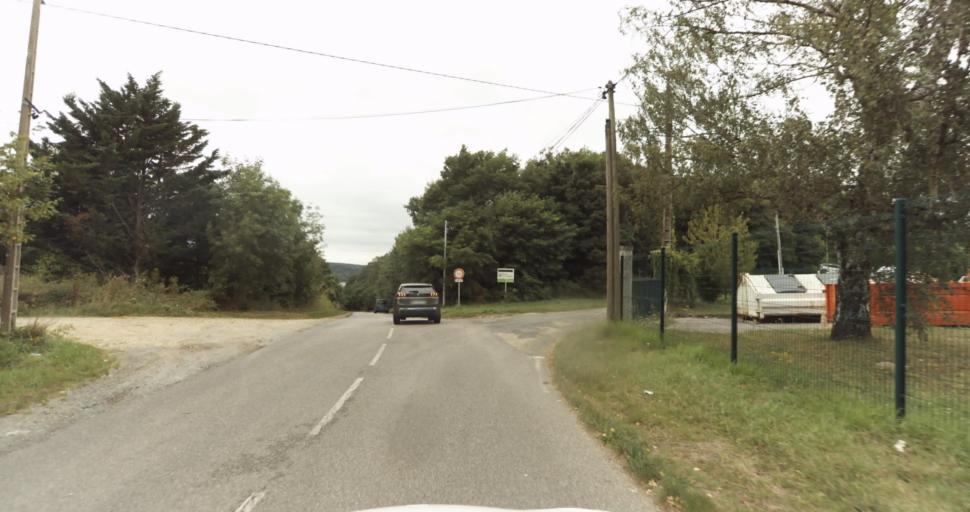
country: FR
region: Haute-Normandie
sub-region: Departement de l'Eure
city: Gravigny
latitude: 49.0407
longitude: 1.1739
